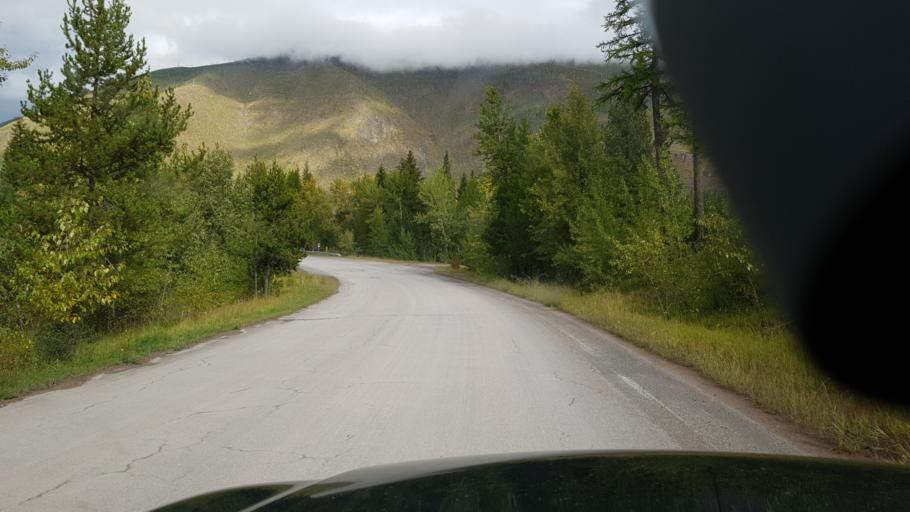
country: US
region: Montana
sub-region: Flathead County
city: Columbia Falls
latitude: 48.6009
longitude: -114.1646
